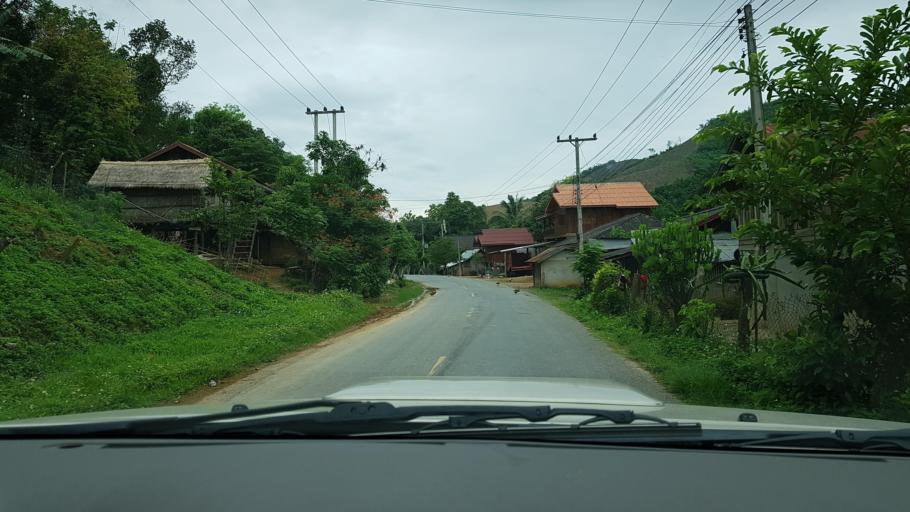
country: LA
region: Loungnamtha
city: Muang Nale
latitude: 20.1896
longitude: 101.5192
